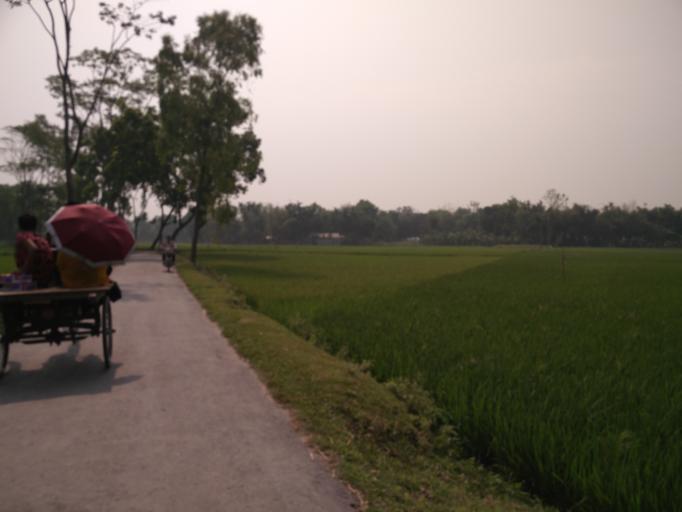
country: BD
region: Dhaka
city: Muktagacha
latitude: 24.9142
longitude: 90.2252
